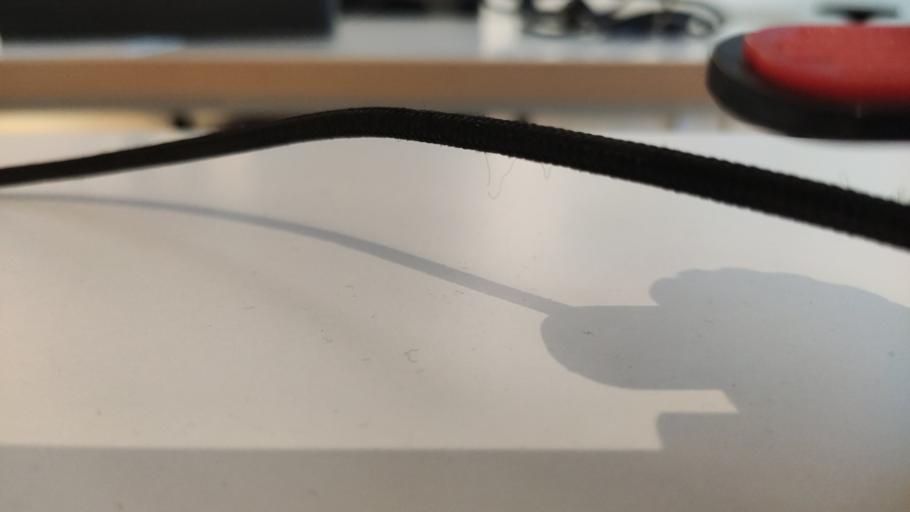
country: RU
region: Moskovskaya
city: Novopetrovskoye
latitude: 55.8788
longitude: 36.4112
